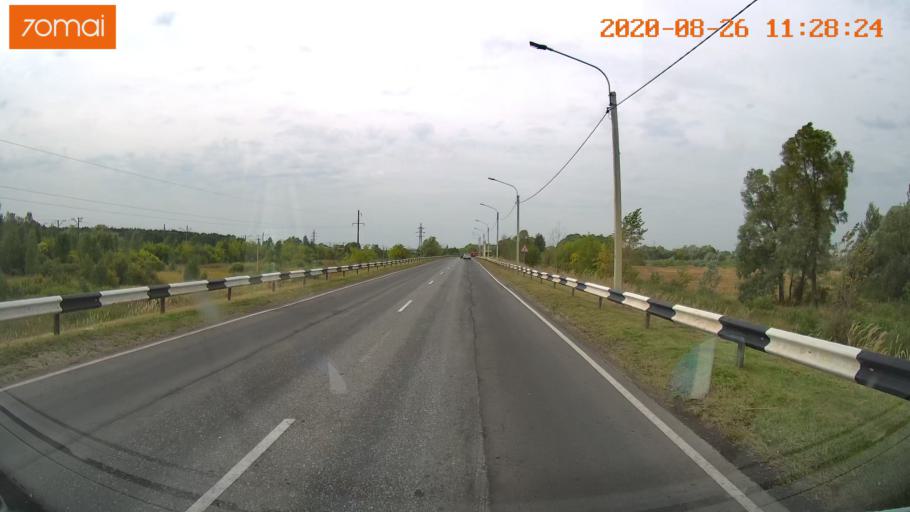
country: RU
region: Rjazan
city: Shilovo
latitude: 54.3233
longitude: 40.9149
